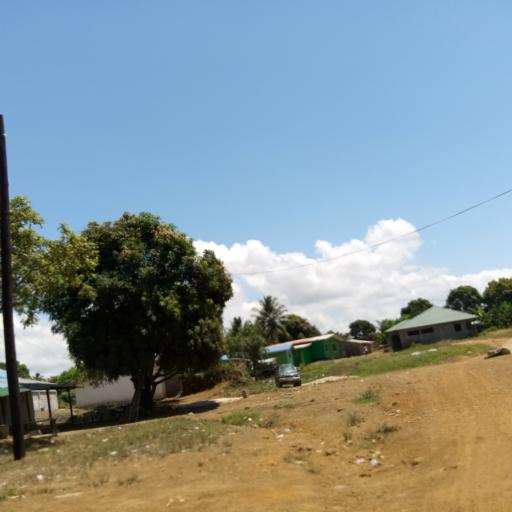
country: LR
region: Montserrado
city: Monrovia
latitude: 6.2512
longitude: -10.6893
